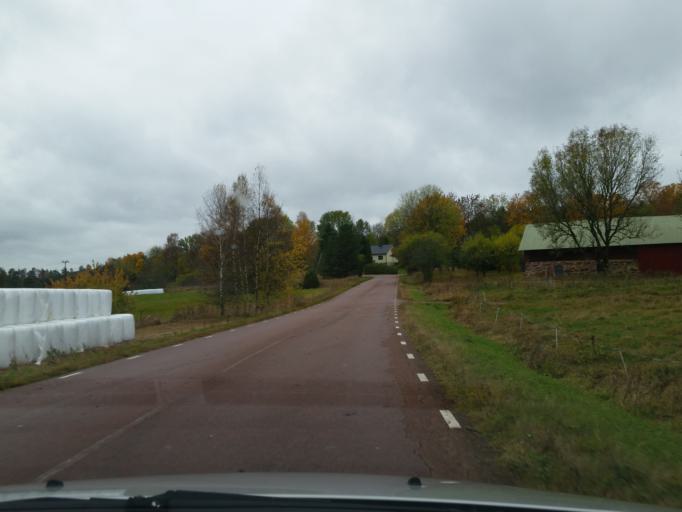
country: AX
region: Alands landsbygd
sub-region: Lumparland
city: Lumparland
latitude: 60.1429
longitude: 20.2701
